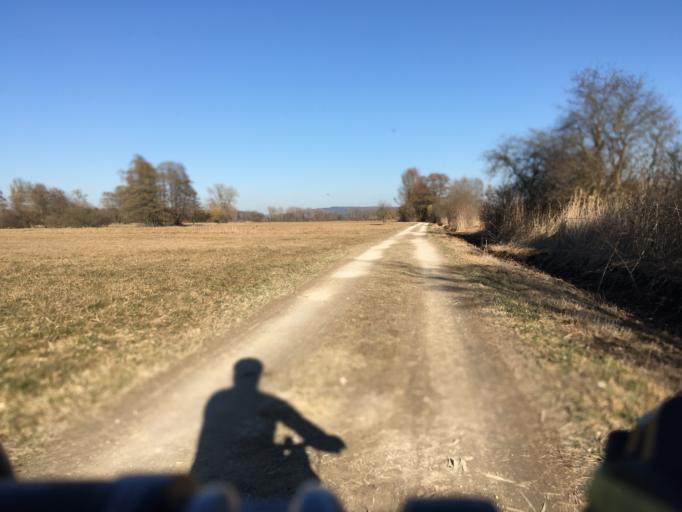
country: DE
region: Baden-Wuerttemberg
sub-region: Freiburg Region
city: Singen
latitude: 47.7833
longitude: 8.8431
